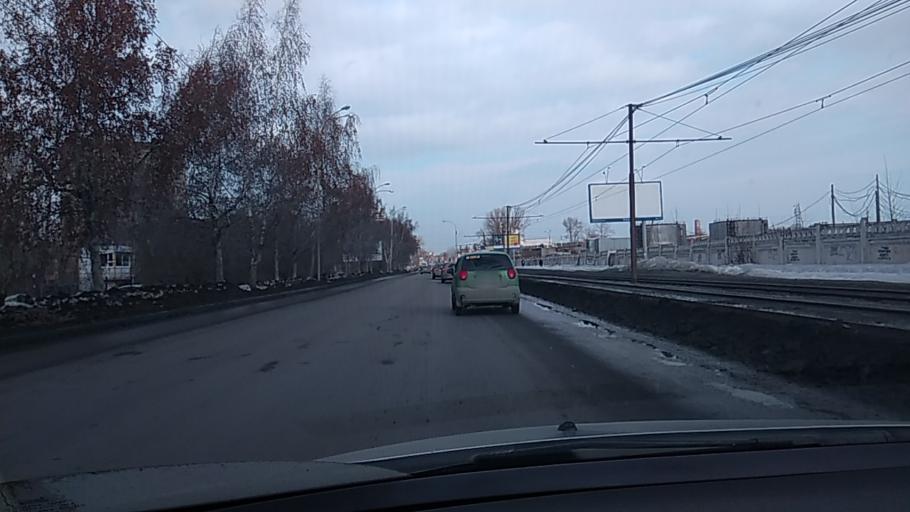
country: RU
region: Sverdlovsk
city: Yekaterinburg
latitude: 56.8594
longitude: 60.6582
